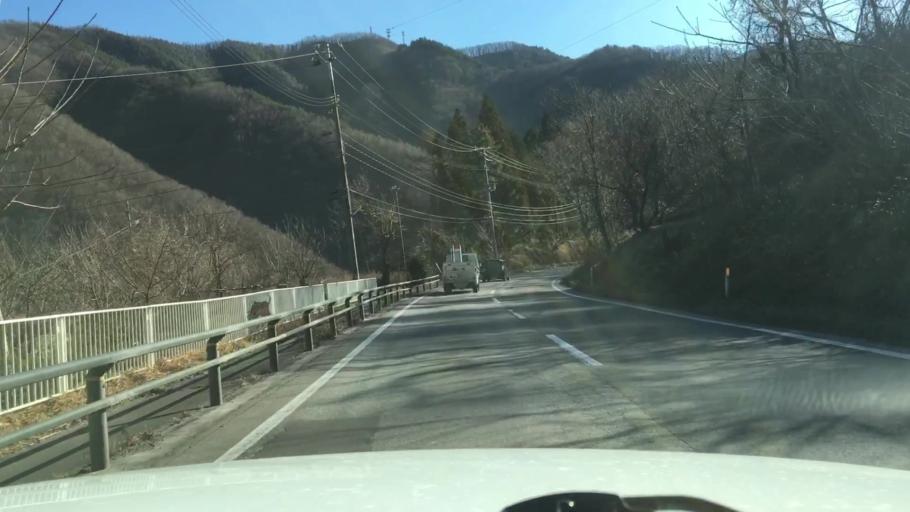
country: JP
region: Iwate
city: Miyako
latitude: 39.6230
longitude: 141.8107
